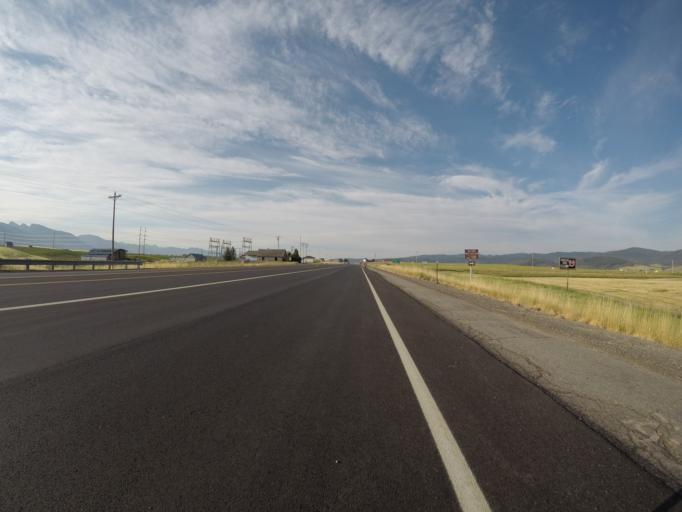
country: US
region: Wyoming
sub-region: Lincoln County
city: Afton
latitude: 42.9838
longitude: -111.0125
